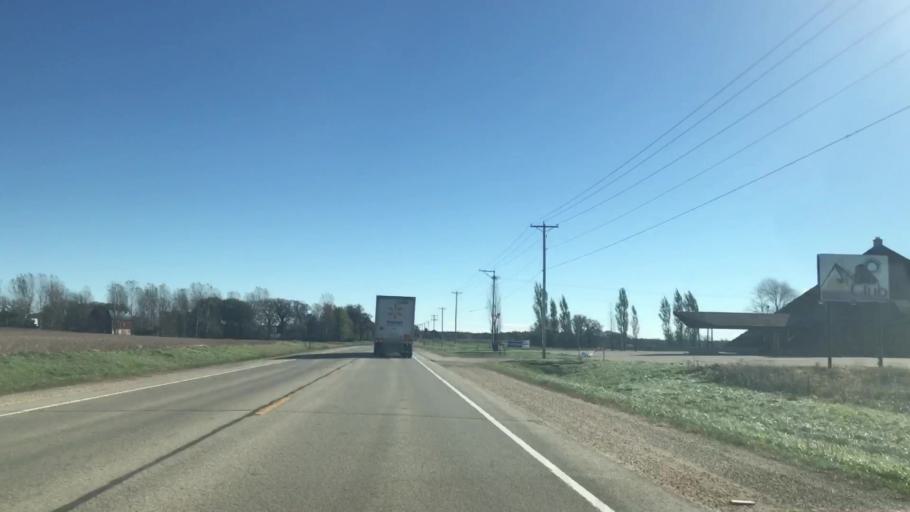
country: US
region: Wisconsin
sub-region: Dodge County
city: Juneau
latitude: 43.4447
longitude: -88.7371
